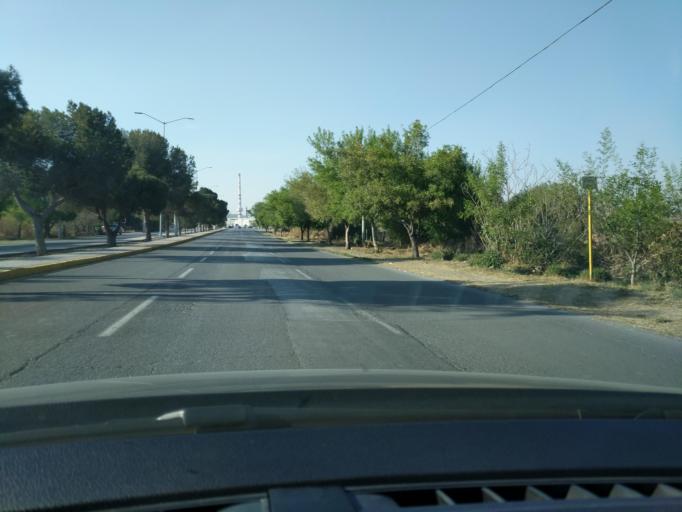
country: MX
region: Coahuila
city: Saltillo
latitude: 25.4749
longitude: -100.9829
